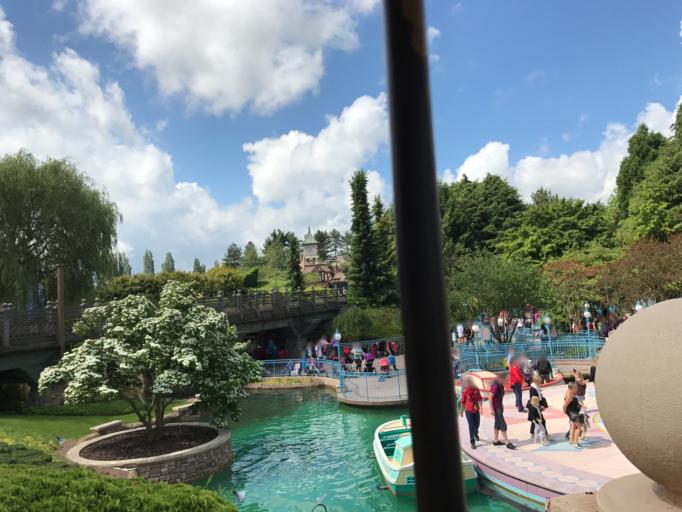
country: FR
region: Ile-de-France
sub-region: Departement de Seine-et-Marne
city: Chessy
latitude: 48.8754
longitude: 2.7748
